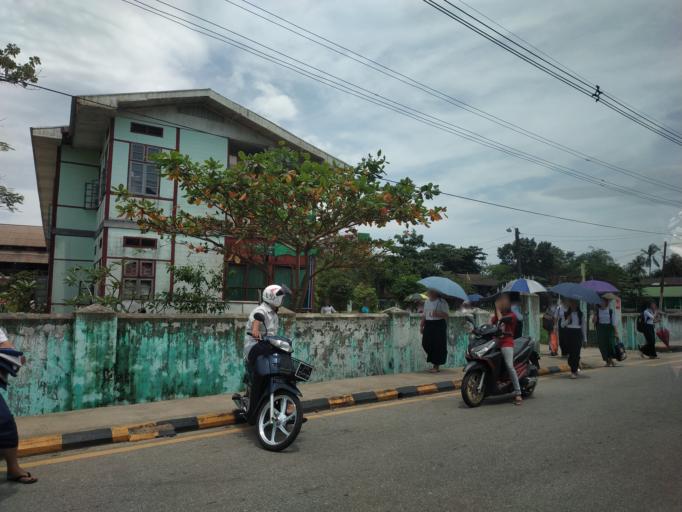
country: MM
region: Tanintharyi
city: Dawei
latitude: 14.0732
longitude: 98.1945
